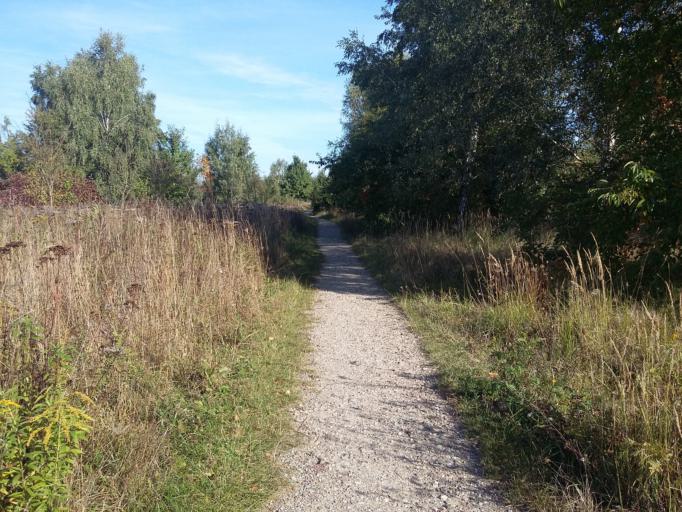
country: PL
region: Lodz Voivodeship
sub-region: Powiat pabianicki
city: Ksawerow
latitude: 51.7320
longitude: 19.3903
